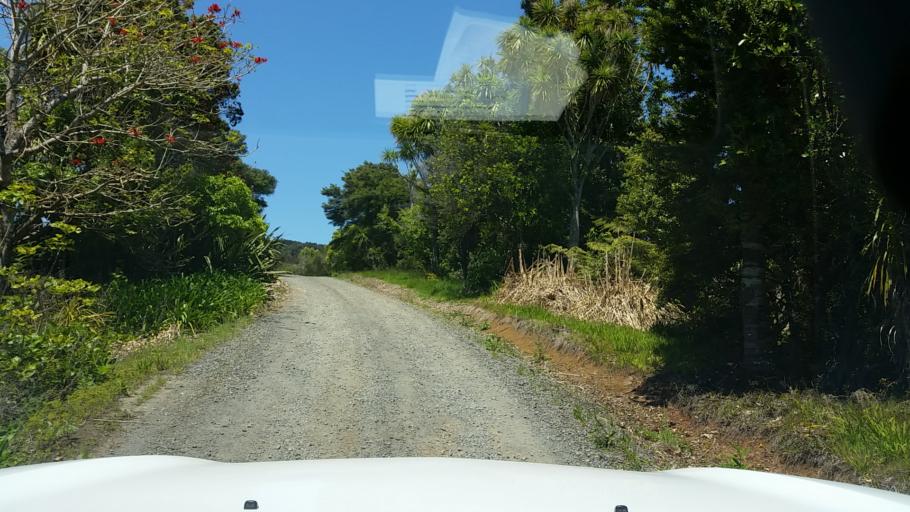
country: NZ
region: Auckland
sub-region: Auckland
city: Muriwai Beach
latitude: -36.8738
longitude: 174.5283
